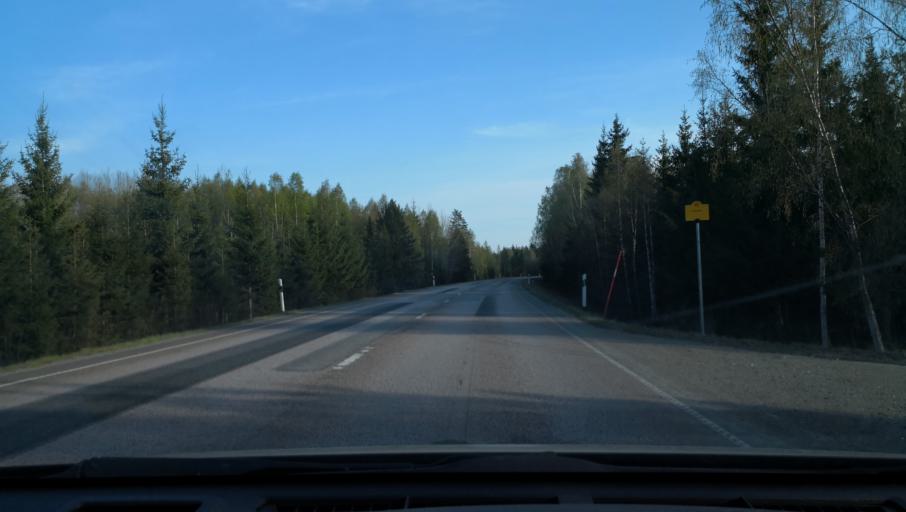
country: SE
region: Uppsala
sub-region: Heby Kommun
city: Heby
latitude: 59.9789
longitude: 16.8360
